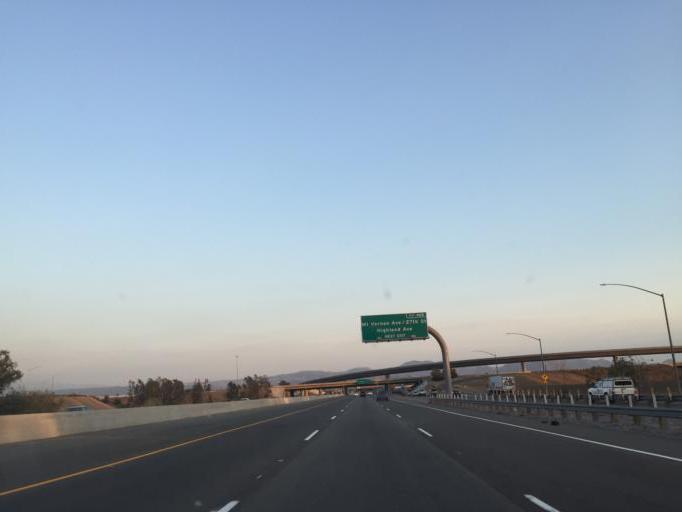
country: US
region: California
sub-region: San Bernardino County
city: Muscoy
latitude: 34.1479
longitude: -117.3215
